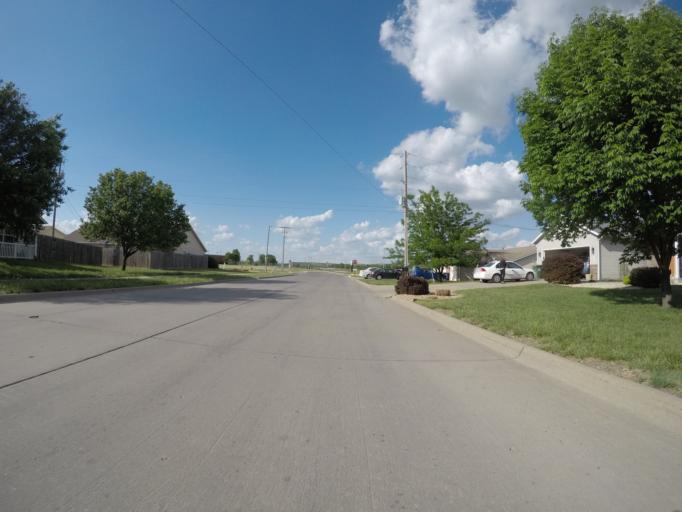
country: US
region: Kansas
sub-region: Riley County
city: Manhattan
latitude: 39.2152
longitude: -96.5704
